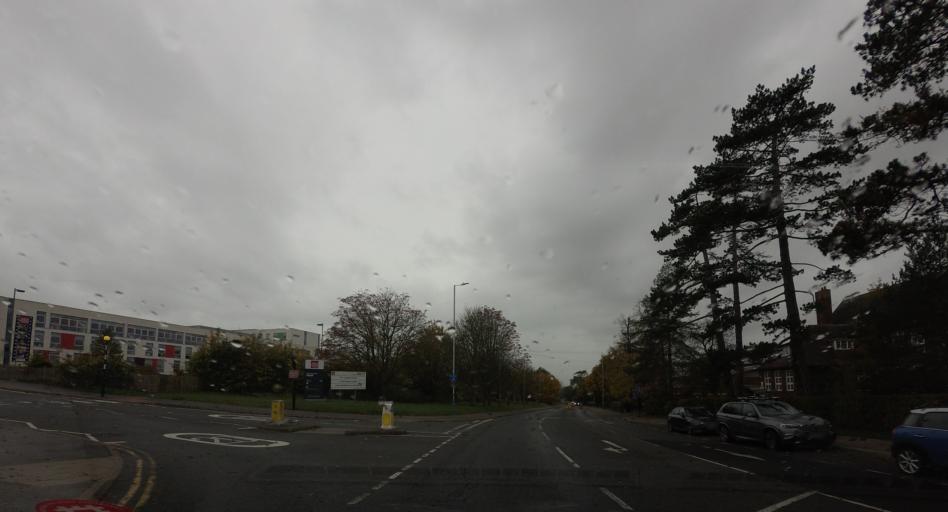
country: GB
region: England
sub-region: Kent
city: Tonbridge
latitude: 51.1876
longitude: 0.2648
